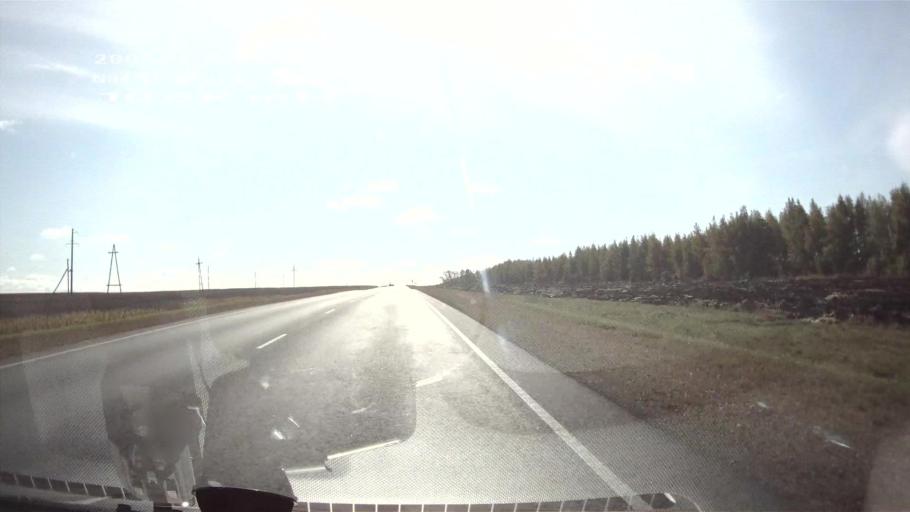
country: RU
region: Ulyanovsk
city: Tsil'na
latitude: 54.5835
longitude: 47.8875
